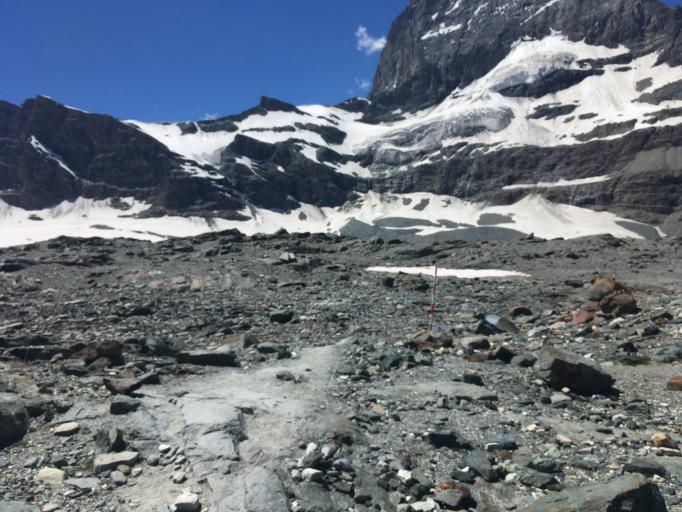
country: CH
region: Valais
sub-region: Visp District
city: Zermatt
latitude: 45.9749
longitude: 7.6970
